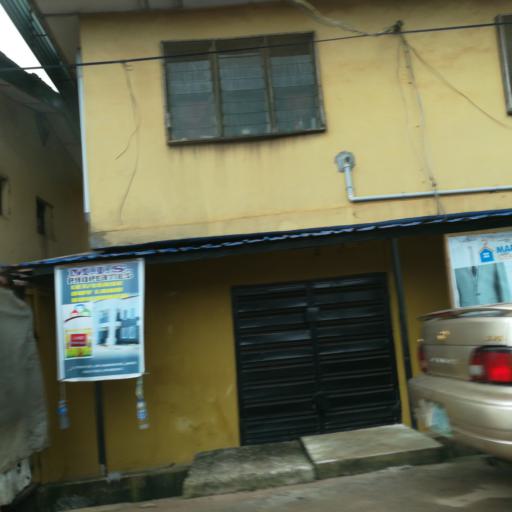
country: NG
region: Lagos
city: Agege
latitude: 6.6095
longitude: 3.3047
